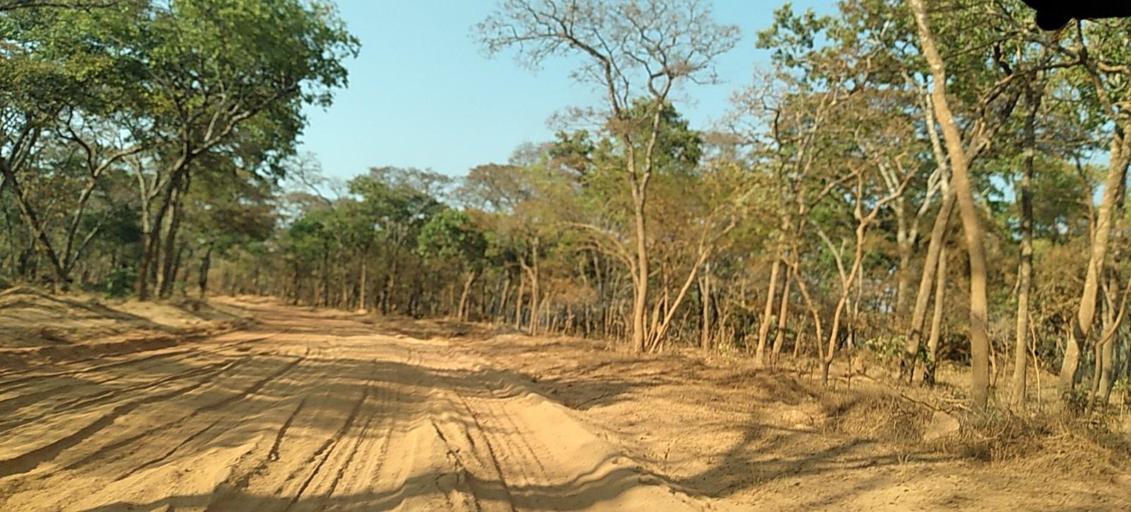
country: ZM
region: North-Western
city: Kasempa
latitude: -13.6039
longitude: 25.9774
